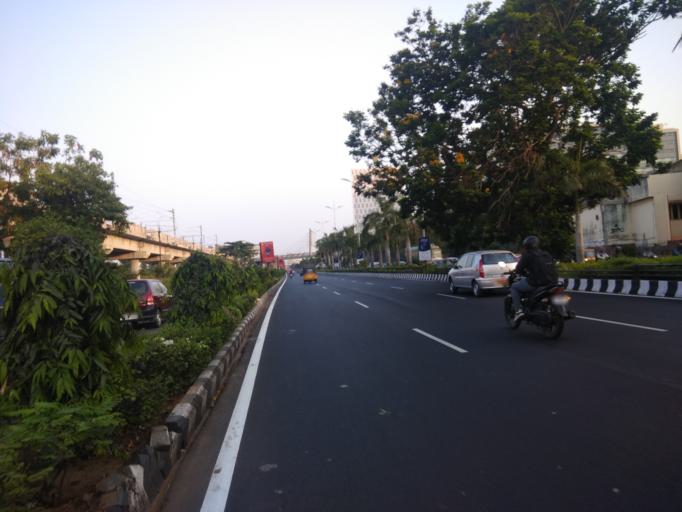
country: IN
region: Tamil Nadu
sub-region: Chennai
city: Gandhi Nagar
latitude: 12.9940
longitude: 80.2499
